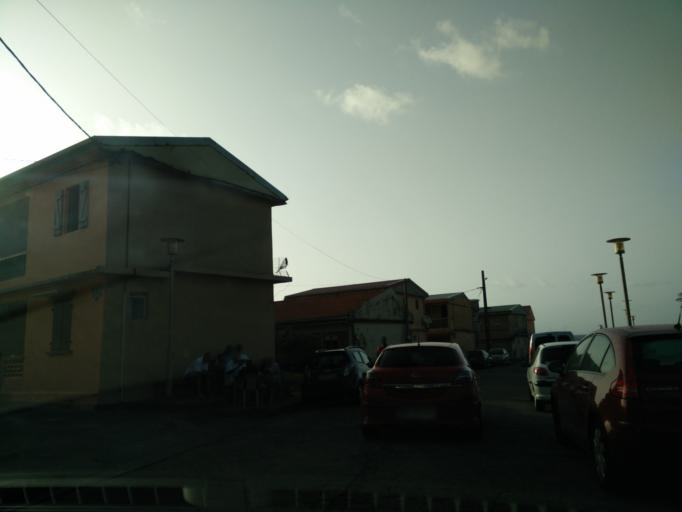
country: MQ
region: Martinique
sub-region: Martinique
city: Basse-Pointe
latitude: 14.8736
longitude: -61.1788
